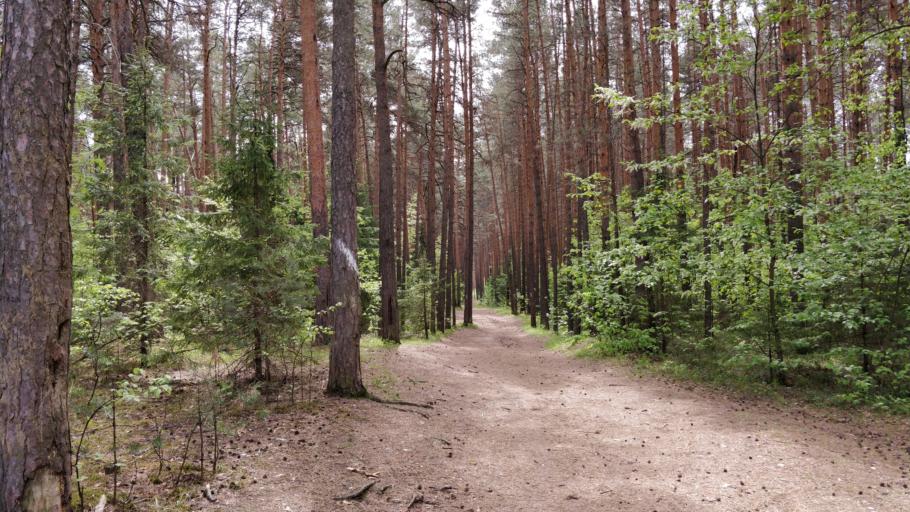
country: RU
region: Perm
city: Kondratovo
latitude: 57.9820
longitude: 56.1372
